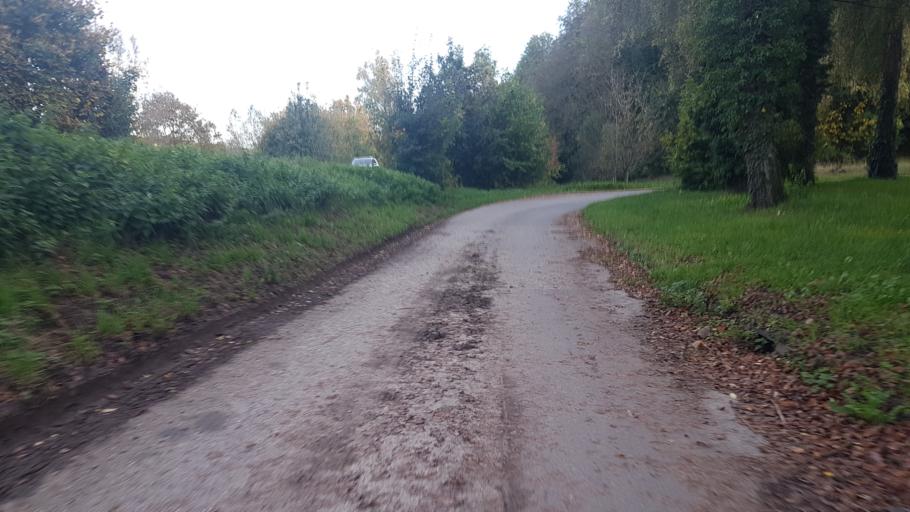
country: DE
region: Baden-Wuerttemberg
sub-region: Karlsruhe Region
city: Neckarzimmern
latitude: 49.3226
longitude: 9.1096
